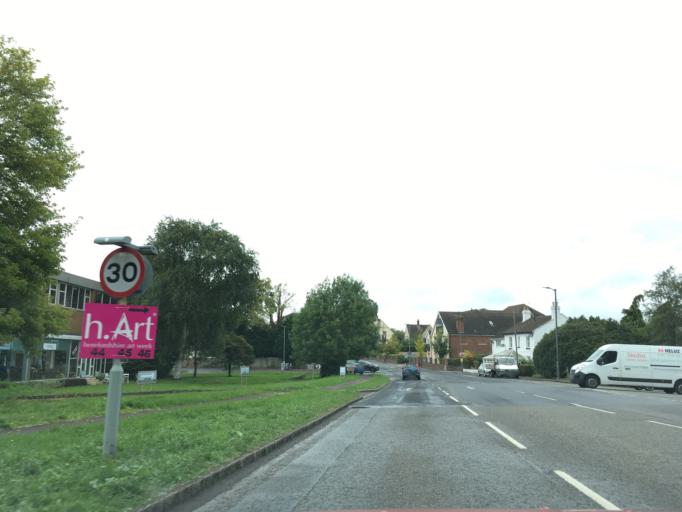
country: GB
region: England
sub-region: Herefordshire
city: Ross on Wye
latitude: 51.9145
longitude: -2.5703
